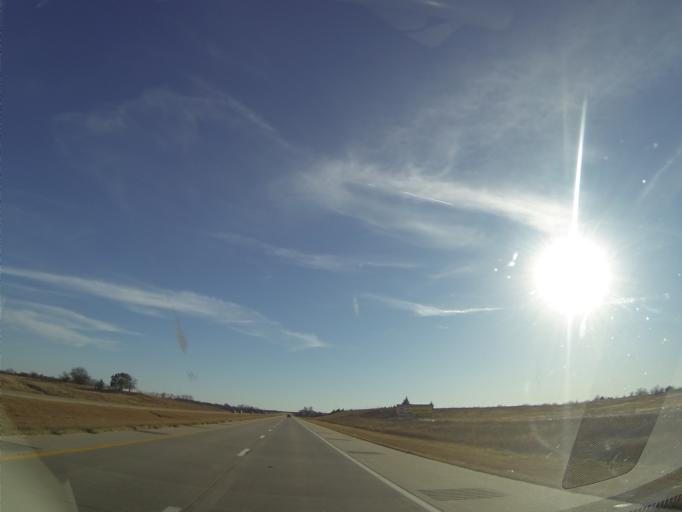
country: US
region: Kansas
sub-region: McPherson County
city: Lindsborg
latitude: 38.6447
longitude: -97.6216
